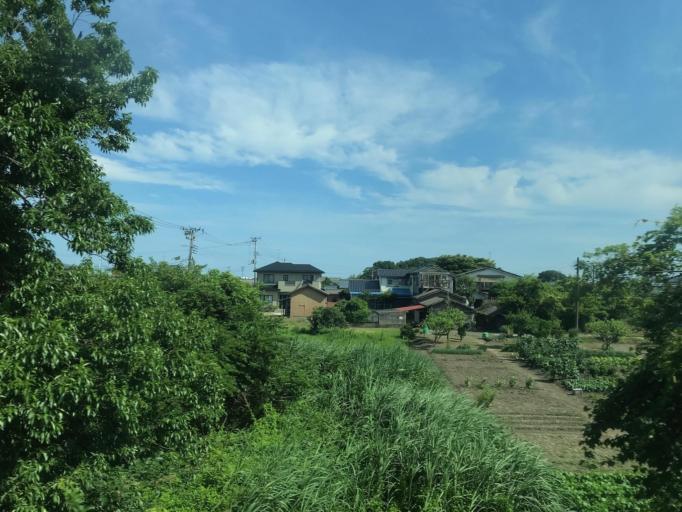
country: JP
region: Niigata
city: Kameda-honcho
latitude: 37.9213
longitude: 139.1533
